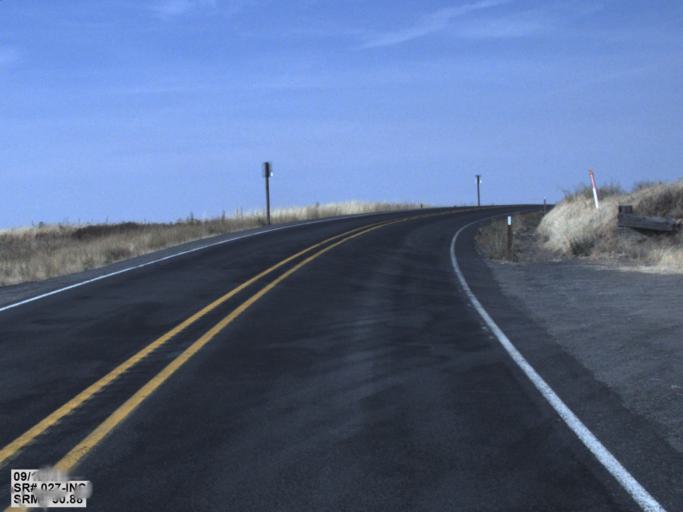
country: US
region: Idaho
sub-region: Benewah County
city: Plummer
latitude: 47.2353
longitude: -117.1183
